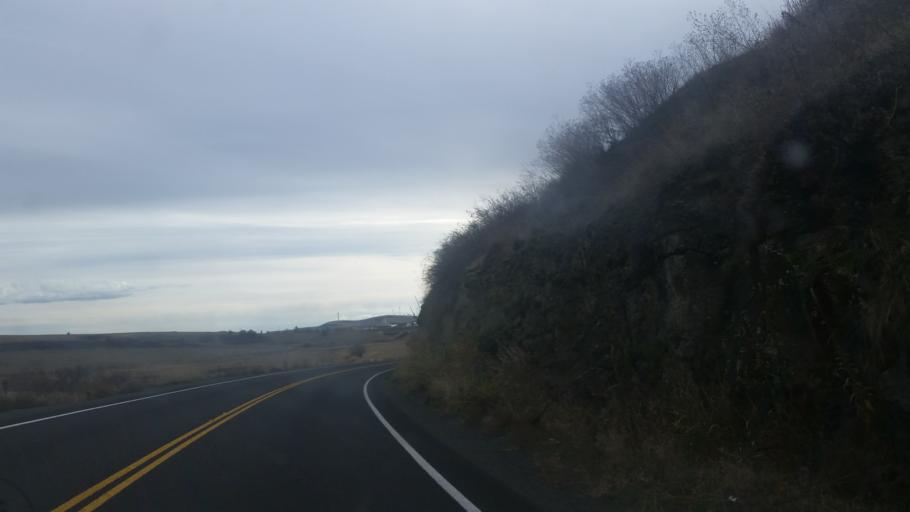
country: US
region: Washington
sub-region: Spokane County
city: Cheney
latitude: 47.2217
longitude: -117.3627
